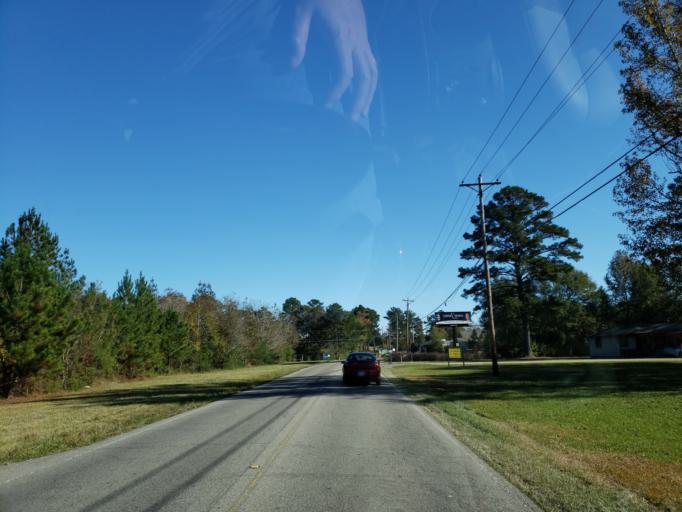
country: US
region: Mississippi
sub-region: Lamar County
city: West Hattiesburg
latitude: 31.3035
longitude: -89.3816
